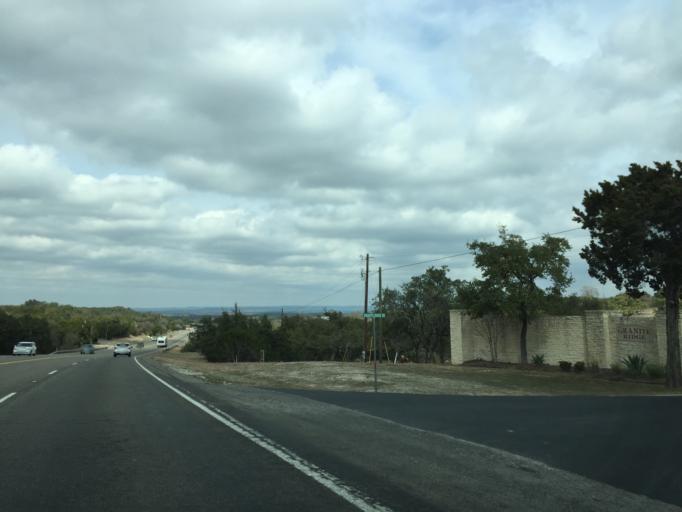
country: US
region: Texas
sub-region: Travis County
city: Briarcliff
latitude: 30.4431
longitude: -98.1474
